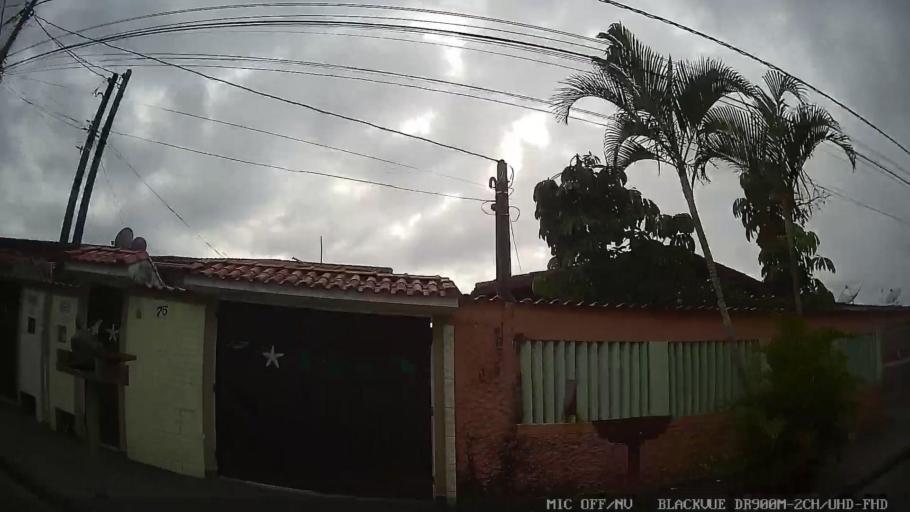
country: BR
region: Sao Paulo
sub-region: Itanhaem
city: Itanhaem
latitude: -24.1975
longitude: -46.8100
